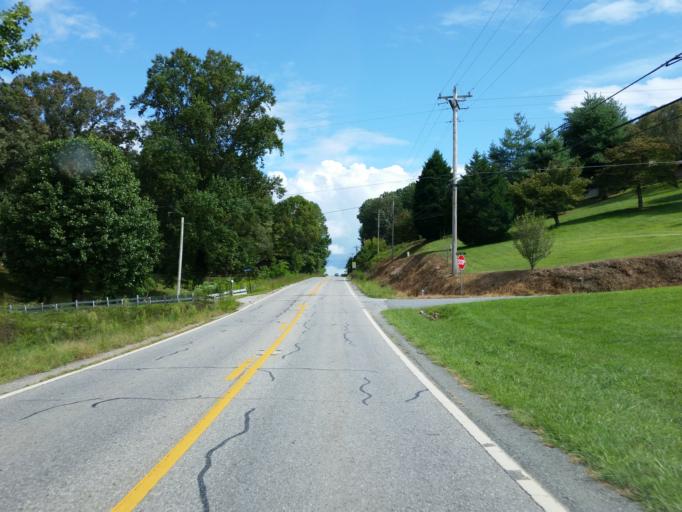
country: US
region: Georgia
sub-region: Fannin County
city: Blue Ridge
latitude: 34.8834
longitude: -84.2534
